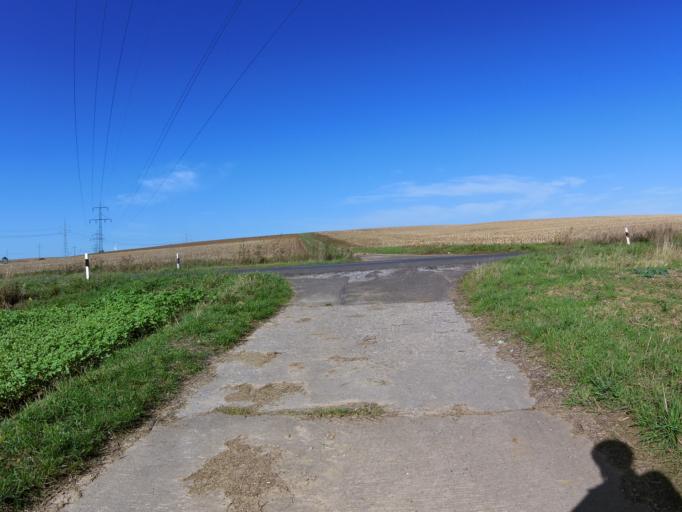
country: DE
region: Bavaria
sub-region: Regierungsbezirk Unterfranken
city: Biebelried
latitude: 49.7597
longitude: 10.0646
